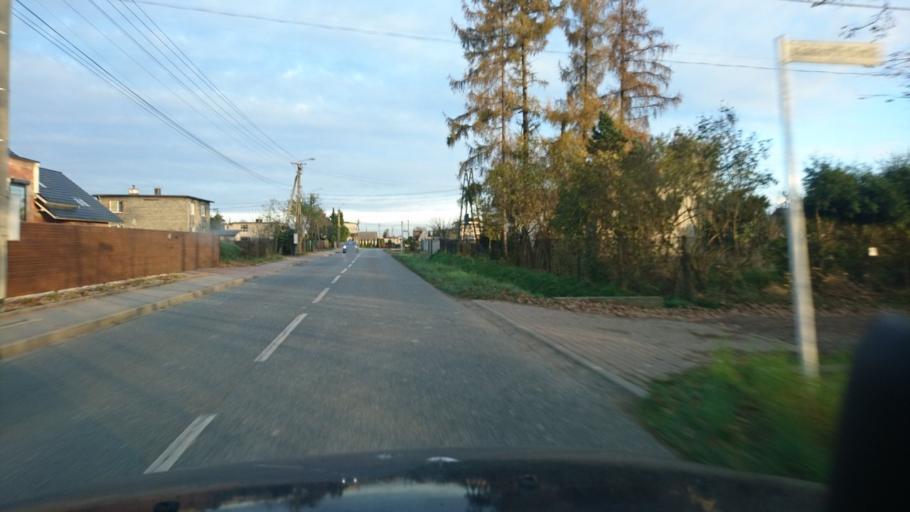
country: PL
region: Silesian Voivodeship
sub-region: Powiat pszczynski
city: Goczalkowice Zdroj
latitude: 49.9440
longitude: 18.9440
